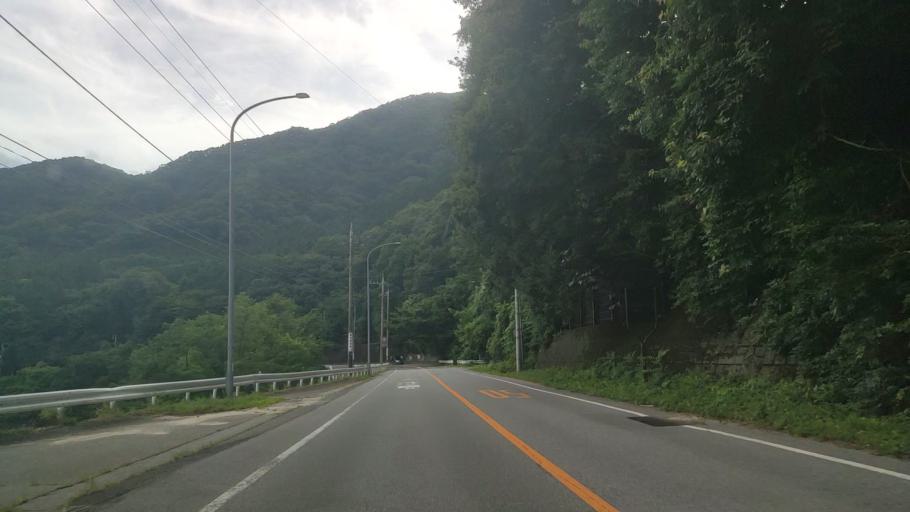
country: JP
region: Gunma
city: Omamacho-omama
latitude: 36.6101
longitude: 139.4036
